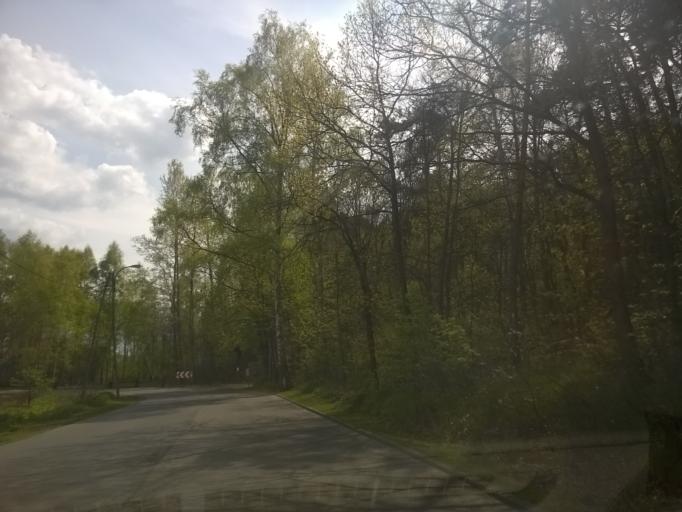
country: PL
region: Masovian Voivodeship
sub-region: Warszawa
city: Kabaty
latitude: 52.1204
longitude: 21.0912
